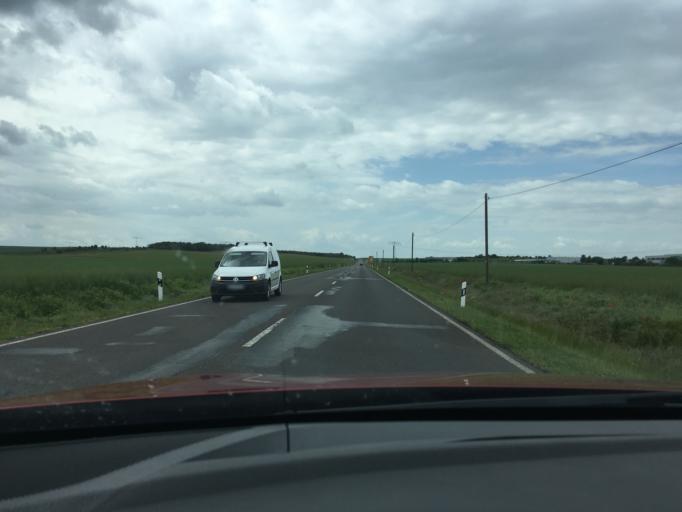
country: DE
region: Saxony-Anhalt
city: Eggersdorf
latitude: 52.0017
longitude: 11.6972
